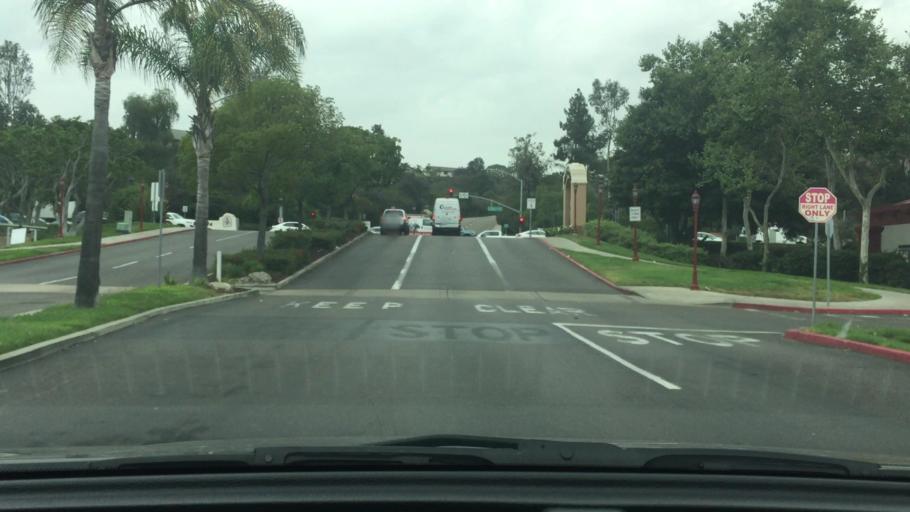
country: US
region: California
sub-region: San Diego County
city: Bonita
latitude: 32.6400
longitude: -117.0498
